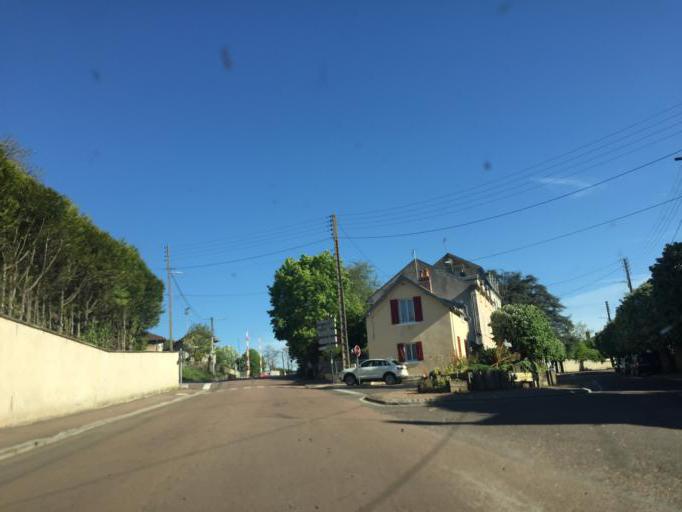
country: FR
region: Bourgogne
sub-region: Departement de la Nievre
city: Clamecy
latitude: 47.4648
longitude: 3.5202
